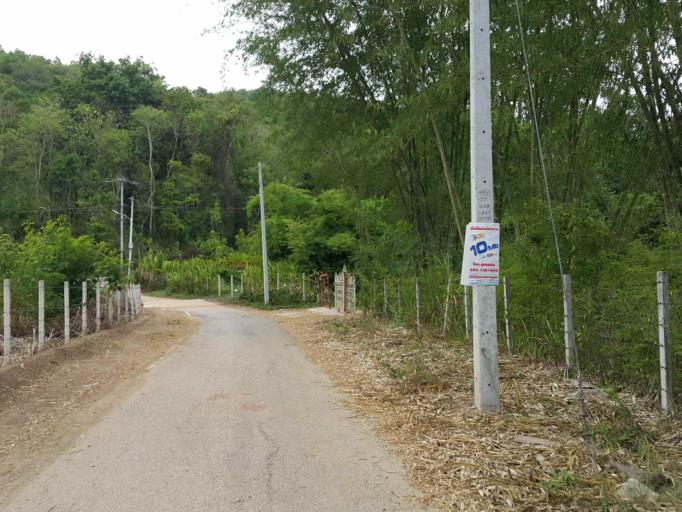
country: TH
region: Chiang Mai
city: Hang Dong
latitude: 18.7560
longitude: 98.9034
